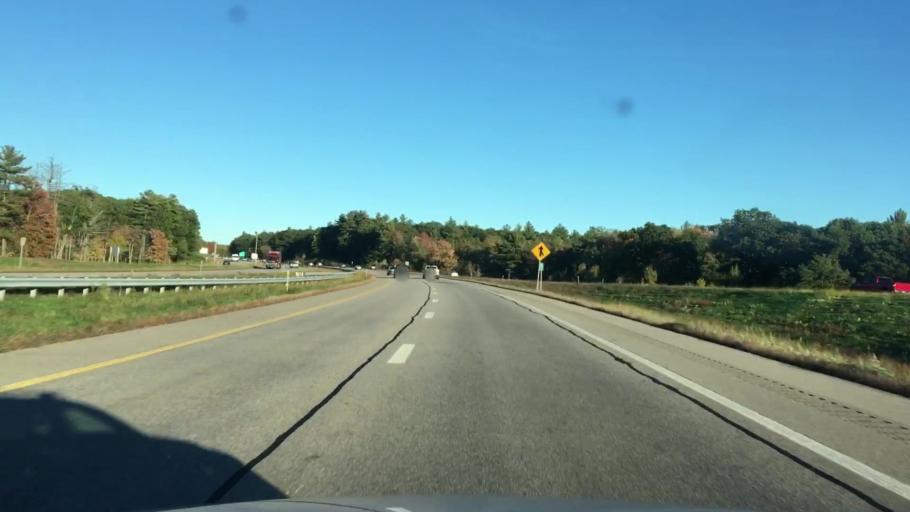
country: US
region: New Hampshire
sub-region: Rockingham County
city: Exeter
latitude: 43.0013
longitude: -70.9742
